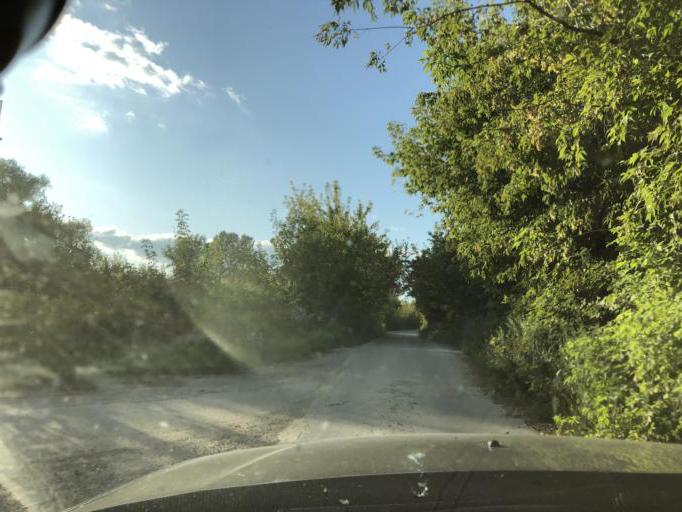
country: RU
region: Tula
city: Mendeleyevskiy
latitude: 54.1836
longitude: 37.5427
